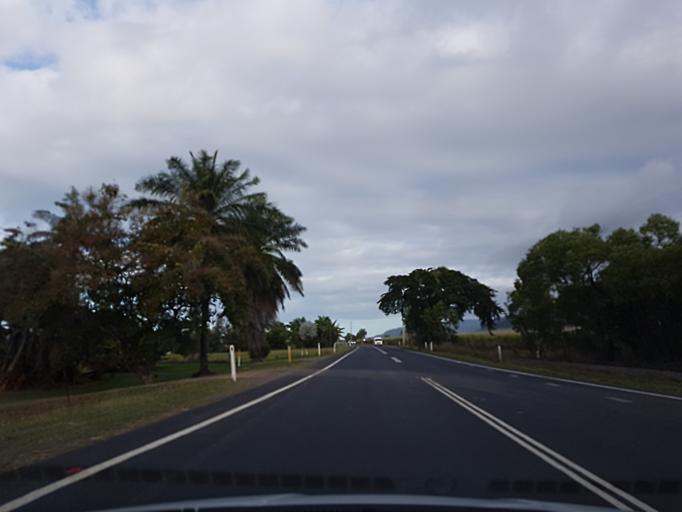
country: AU
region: Queensland
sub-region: Cairns
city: Port Douglas
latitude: -16.4924
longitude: 145.4222
